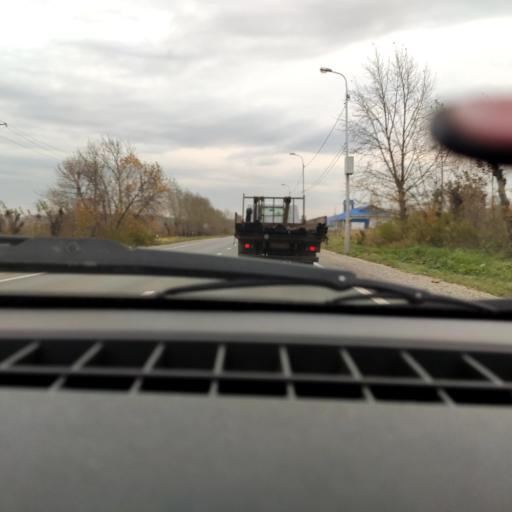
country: RU
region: Bashkortostan
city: Ufa
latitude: 54.8514
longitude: 56.1172
